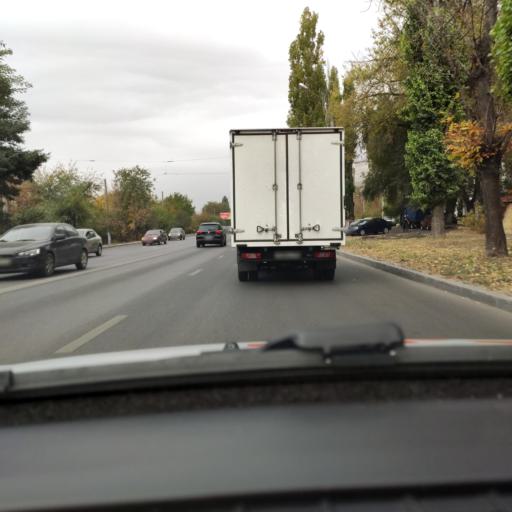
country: RU
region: Voronezj
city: Voronezh
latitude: 51.6940
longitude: 39.2016
